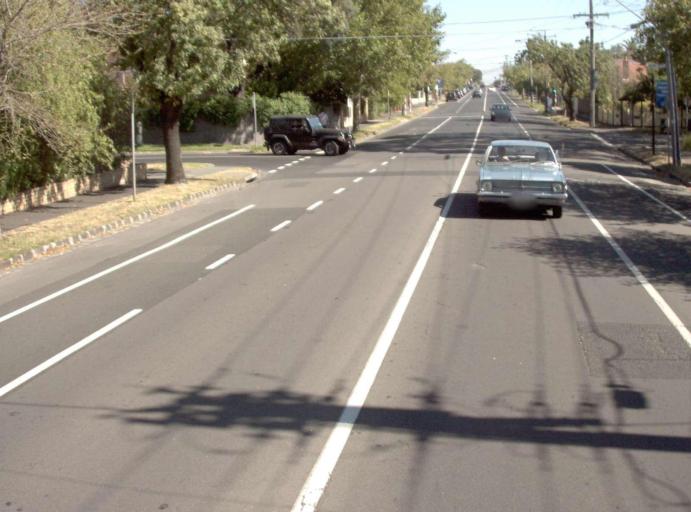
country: AU
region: Victoria
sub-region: Bayside
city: Hampton
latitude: -37.9257
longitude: 145.0047
